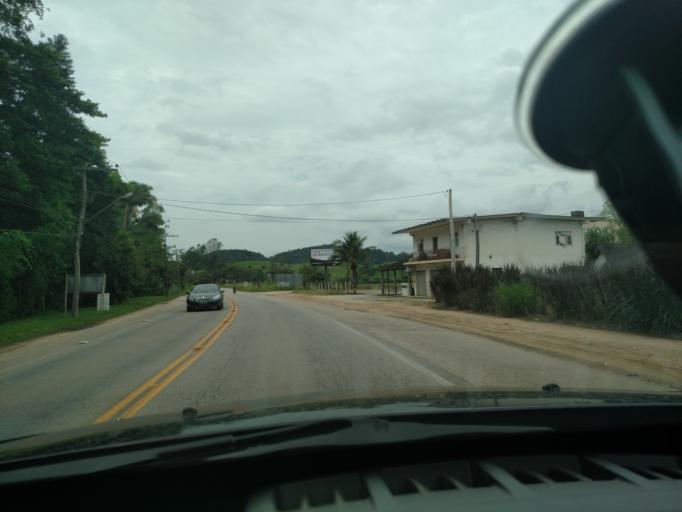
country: BR
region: Santa Catarina
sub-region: Gaspar
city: Gaspar
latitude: -26.9278
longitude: -48.8903
